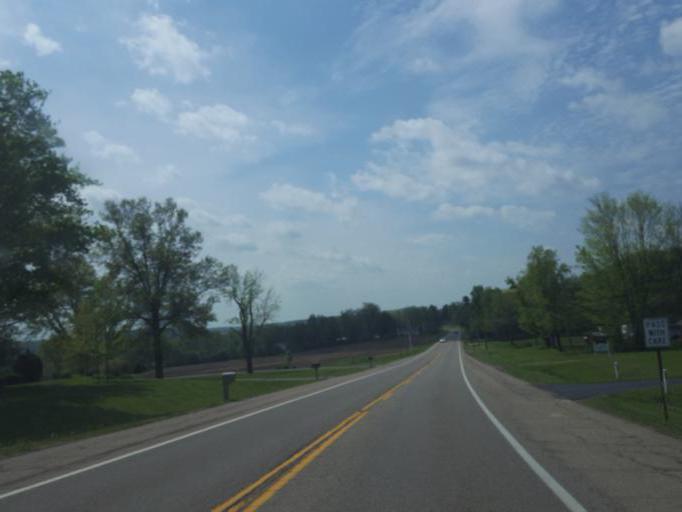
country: US
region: Ohio
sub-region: Licking County
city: Heath
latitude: 40.0110
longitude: -82.4041
